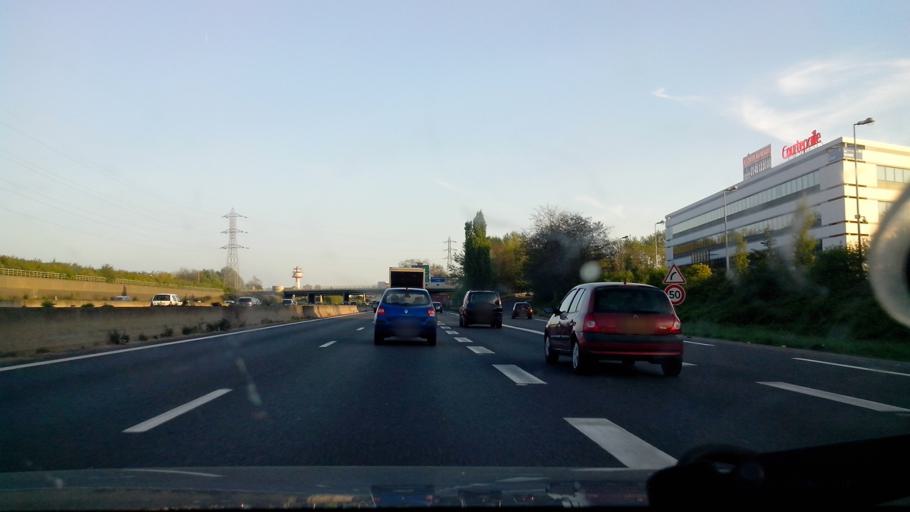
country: FR
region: Ile-de-France
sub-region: Departement de l'Essonne
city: Lisses
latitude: 48.6140
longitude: 2.4301
